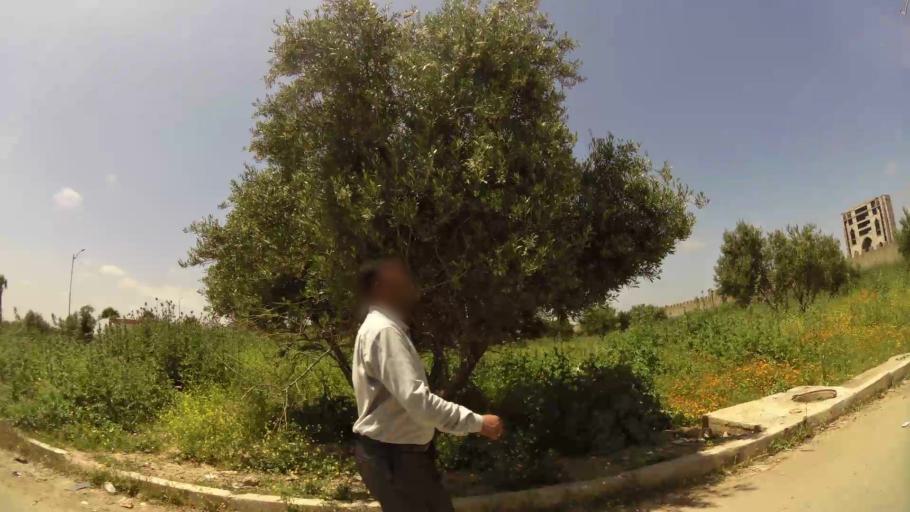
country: MA
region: Fes-Boulemane
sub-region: Fes
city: Fes
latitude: 34.0483
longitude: -5.0437
